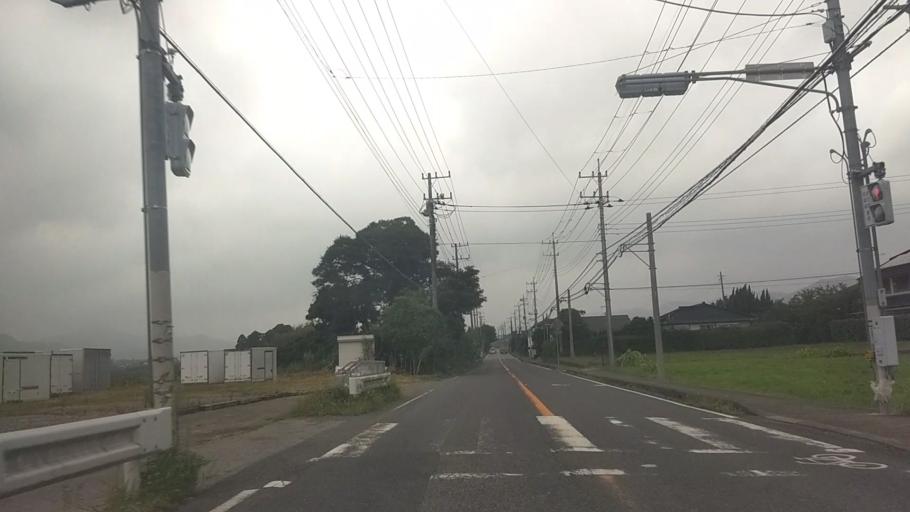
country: JP
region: Chiba
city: Kawaguchi
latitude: 35.1221
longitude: 140.0656
